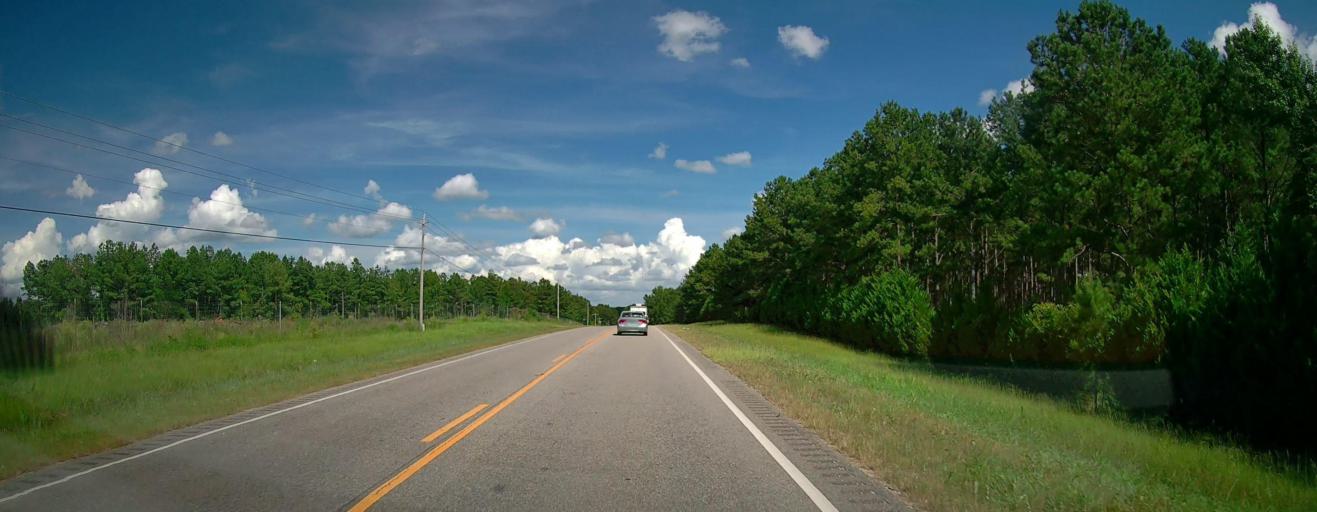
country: US
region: Alabama
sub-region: Macon County
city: Tuskegee
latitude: 32.3821
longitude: -85.8032
